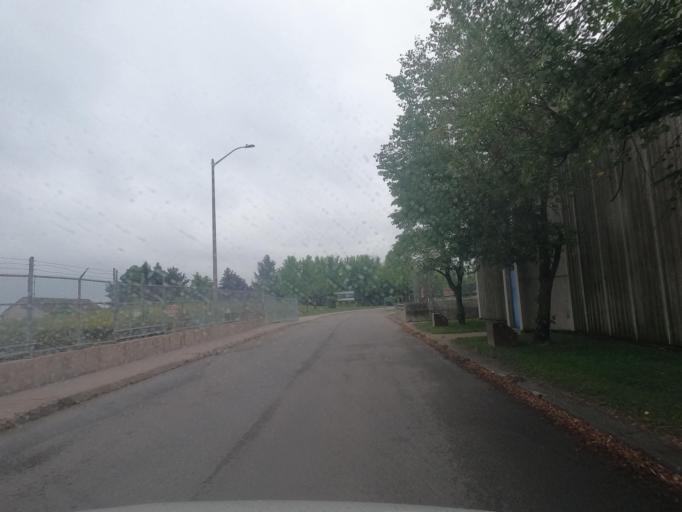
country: CA
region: Ontario
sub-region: Algoma
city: Sault Ste. Marie
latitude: 46.5147
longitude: -84.3471
